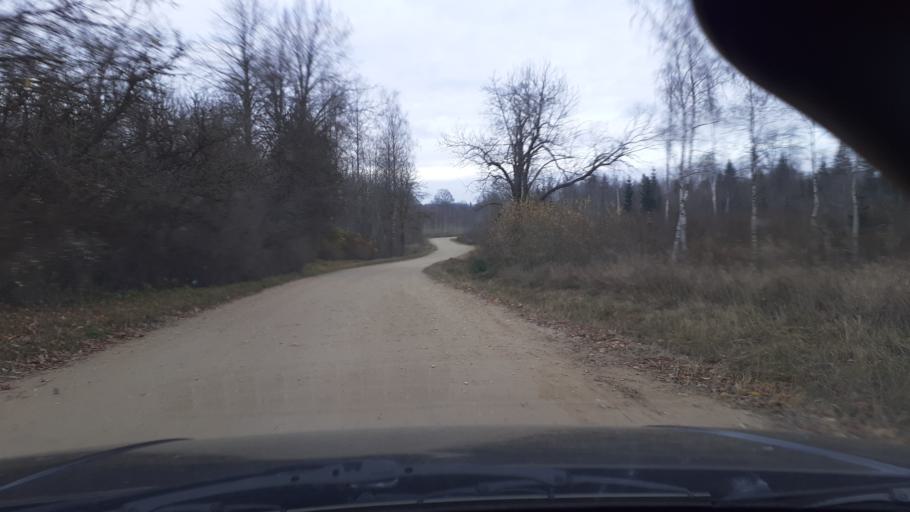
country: LV
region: Alsunga
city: Alsunga
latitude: 56.9498
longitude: 21.6430
